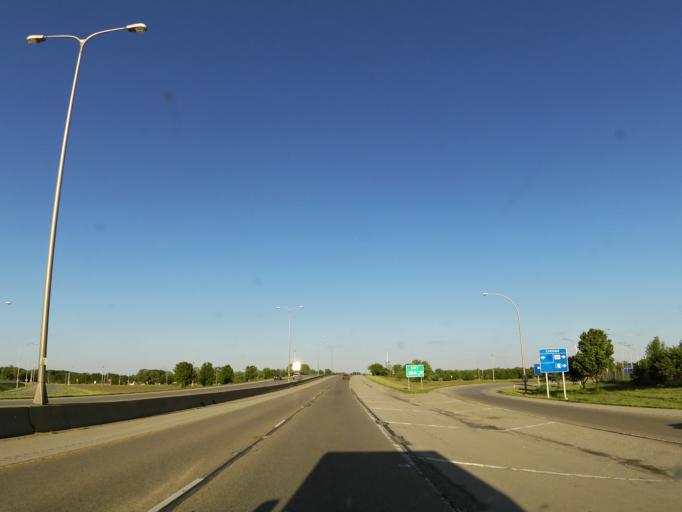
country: US
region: Illinois
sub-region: Champaign County
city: Urbana
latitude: 40.1345
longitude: -88.1997
